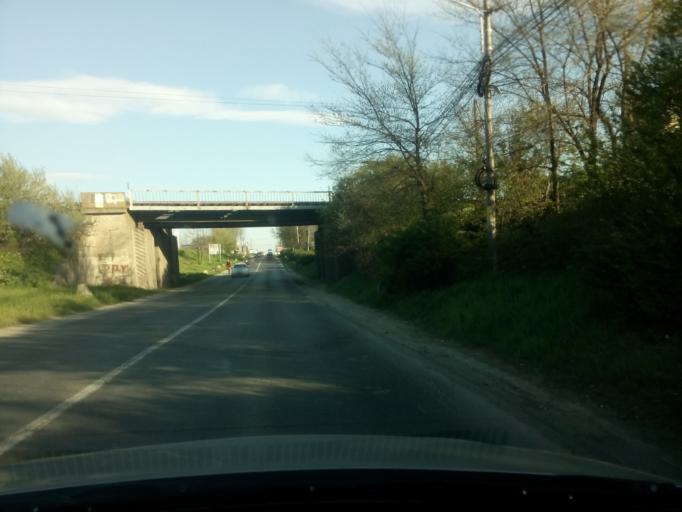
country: RO
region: Ilfov
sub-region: Comuna Mogosoaia
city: Mogosoaia
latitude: 44.5210
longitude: 26.0090
